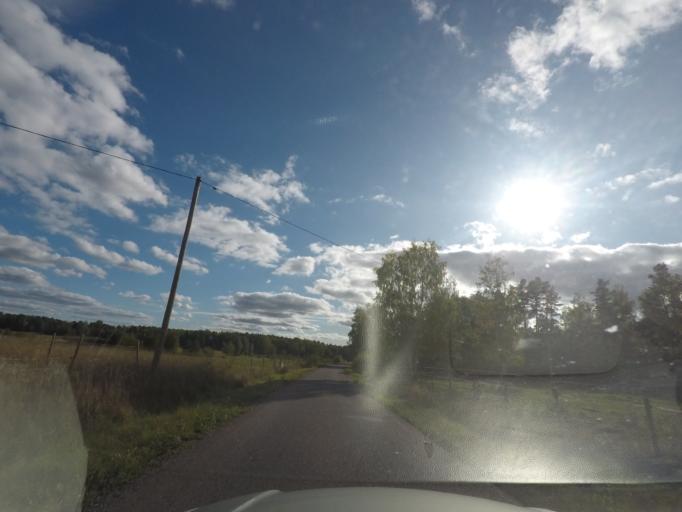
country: SE
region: Vaestmanland
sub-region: Hallstahammars Kommun
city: Kolback
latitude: 59.5025
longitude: 16.1914
